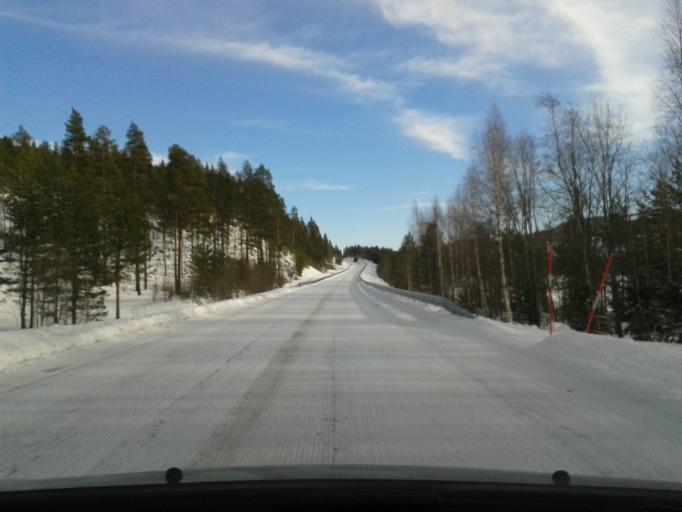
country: SE
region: Vaesterbotten
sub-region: Asele Kommun
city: Asele
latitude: 64.3196
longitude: 17.1188
